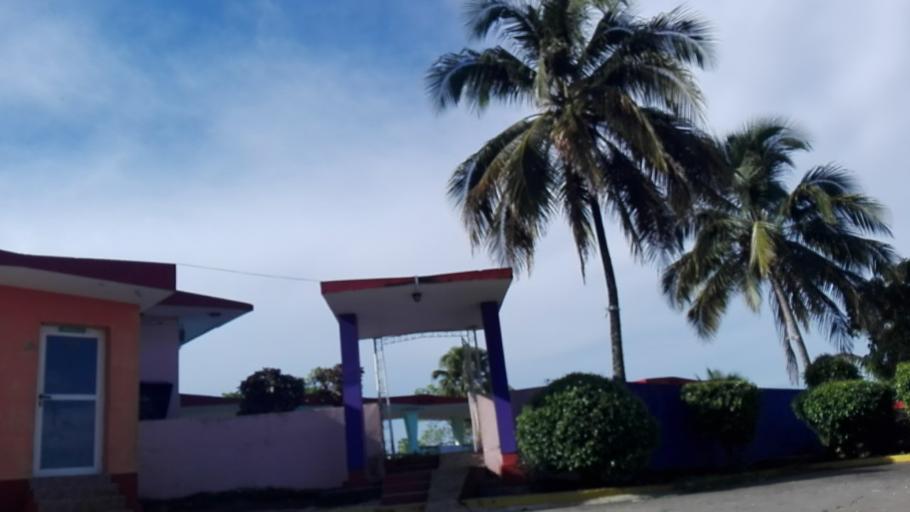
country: CU
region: Granma
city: Bartolome Maso
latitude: 20.1577
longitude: -76.9504
